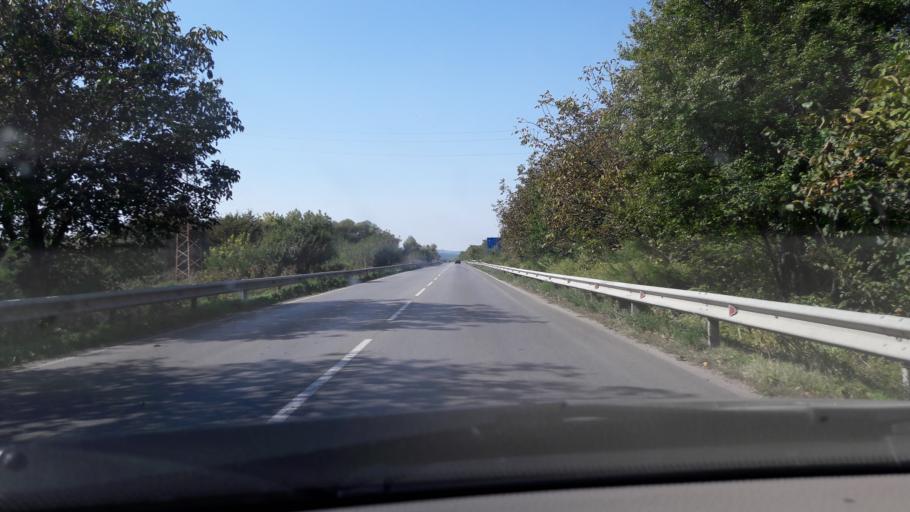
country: BG
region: Razgrad
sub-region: Obshtina Razgrad
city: Razgrad
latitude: 43.5465
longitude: 26.4888
